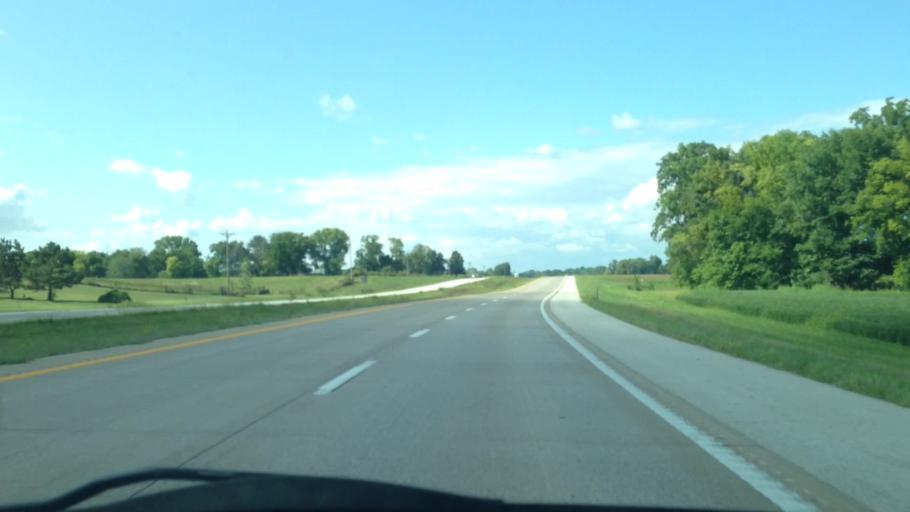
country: US
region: Missouri
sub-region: Lewis County
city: Canton
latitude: 40.2473
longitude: -91.5396
